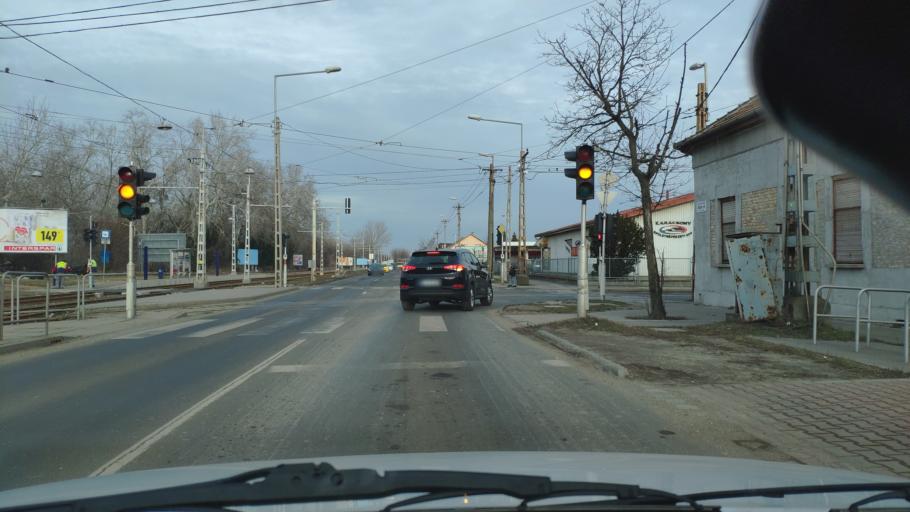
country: HU
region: Budapest
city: Budapest XX. keruelet
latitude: 47.4486
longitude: 19.1043
